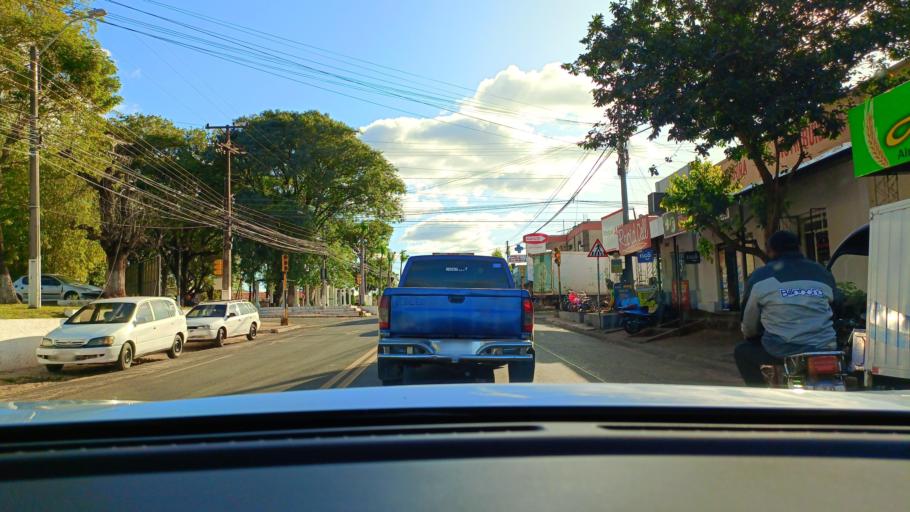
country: PY
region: San Pedro
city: Guayaybi
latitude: -24.6631
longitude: -56.4414
